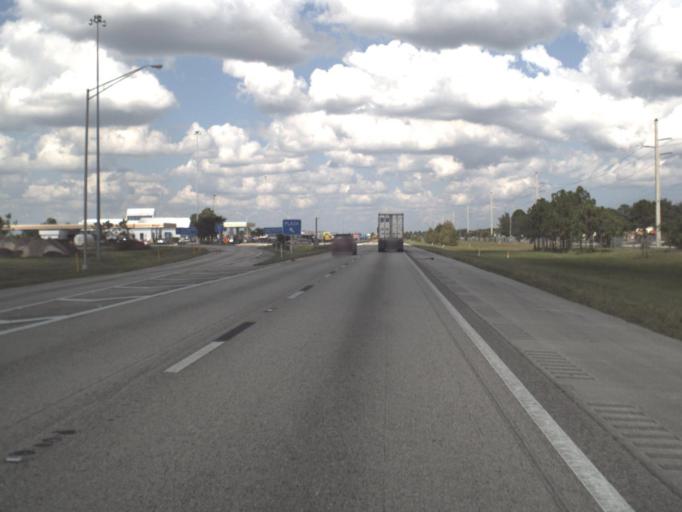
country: US
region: Florida
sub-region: Saint Lucie County
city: Port Saint Lucie
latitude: 27.2991
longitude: -80.3711
